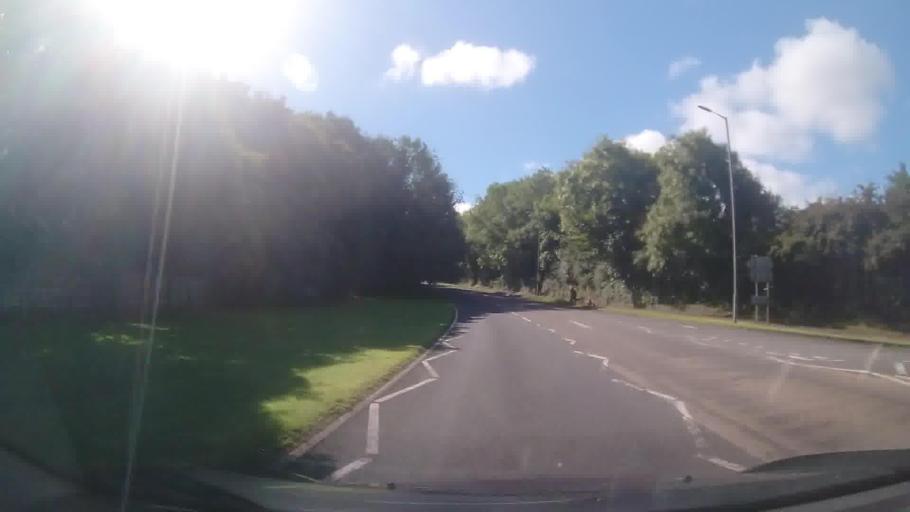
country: GB
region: Wales
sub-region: Pembrokeshire
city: Penally
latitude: 51.6688
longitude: -4.7239
